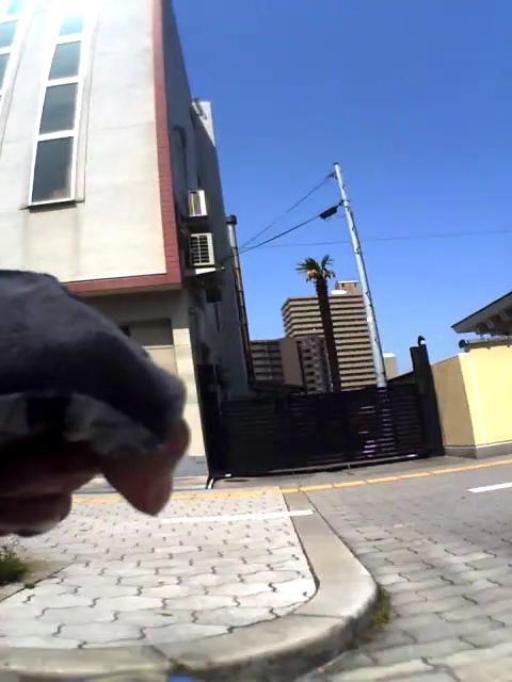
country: JP
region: Osaka
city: Osaka-shi
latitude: 34.6709
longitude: 135.5165
